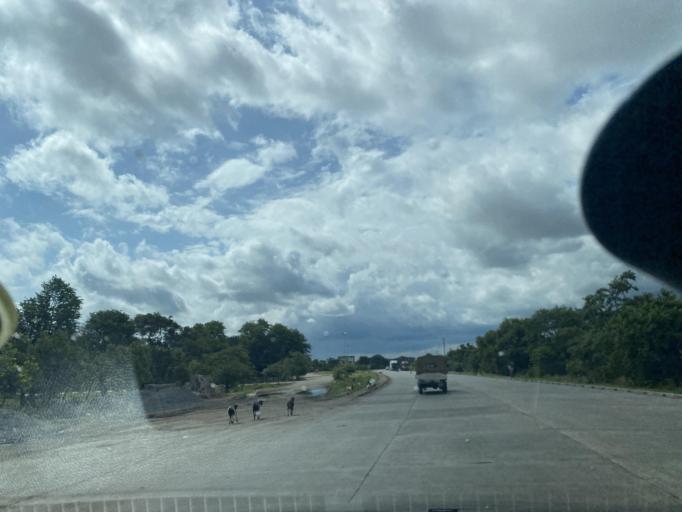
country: ZM
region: Lusaka
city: Kafue
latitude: -15.8465
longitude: 28.2454
